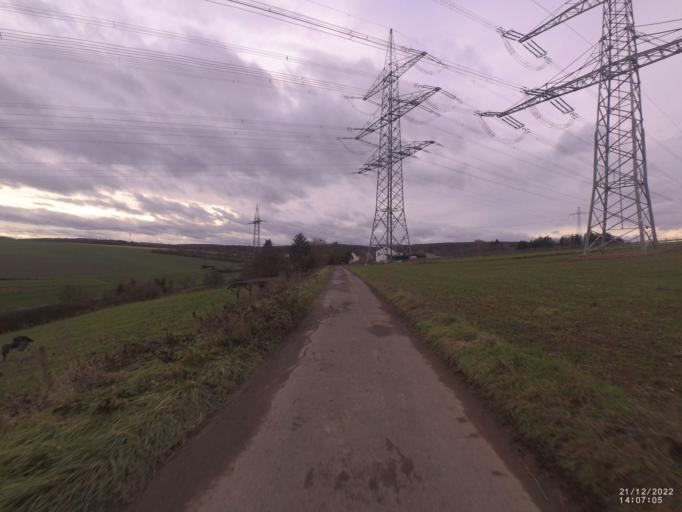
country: DE
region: Rheinland-Pfalz
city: Waldorf
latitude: 50.5029
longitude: 7.2411
